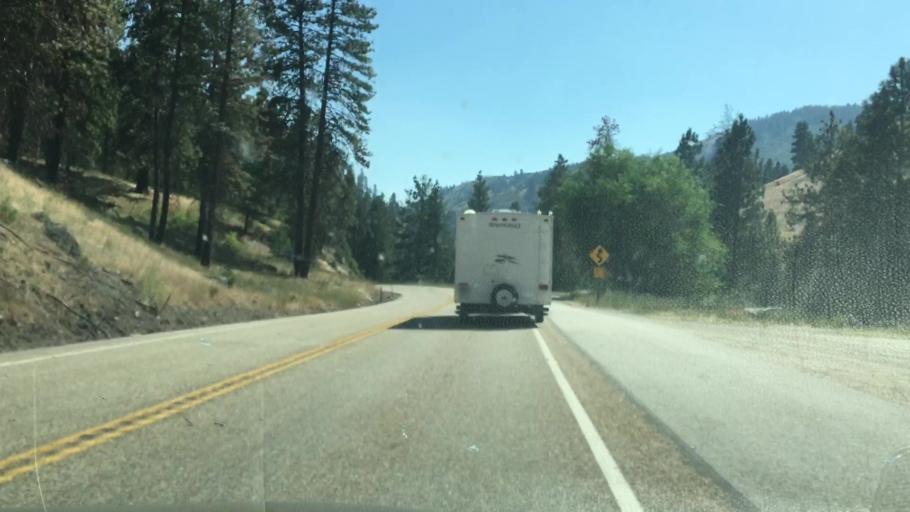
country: US
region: Idaho
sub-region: Boise County
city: Idaho City
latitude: 44.0682
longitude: -116.1198
